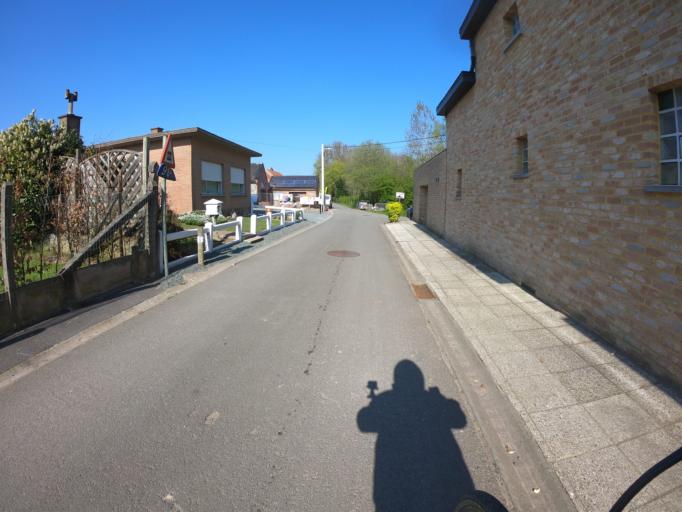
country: BE
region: Flanders
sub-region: Provincie Oost-Vlaanderen
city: Ninove
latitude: 50.8165
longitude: 3.9808
